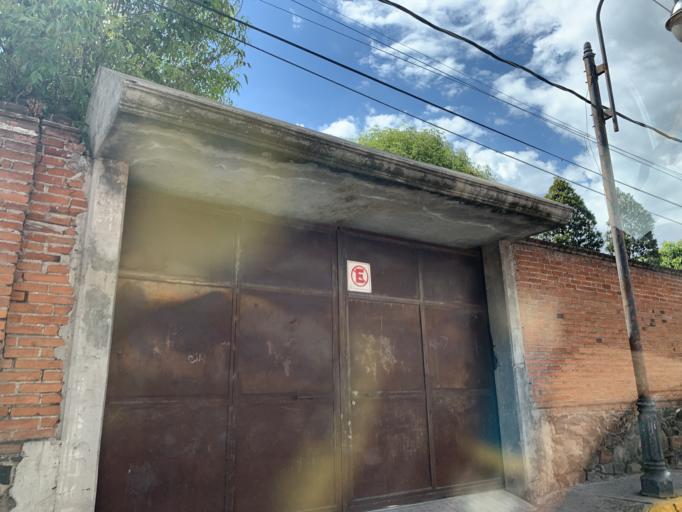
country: MX
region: Puebla
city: San Andres Cholula
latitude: 19.0493
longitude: -98.2983
